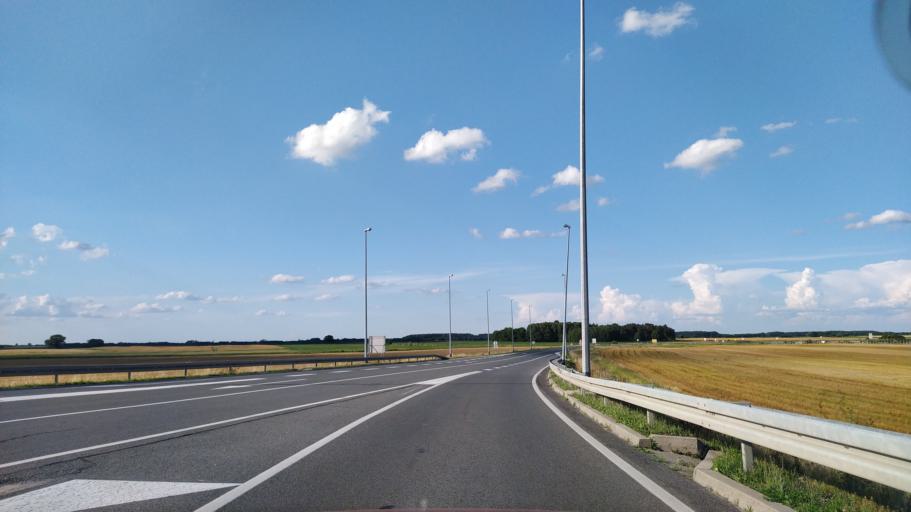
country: HR
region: Virovitick-Podravska
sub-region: Grad Virovitica
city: Virovitica
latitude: 45.8443
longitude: 17.3529
